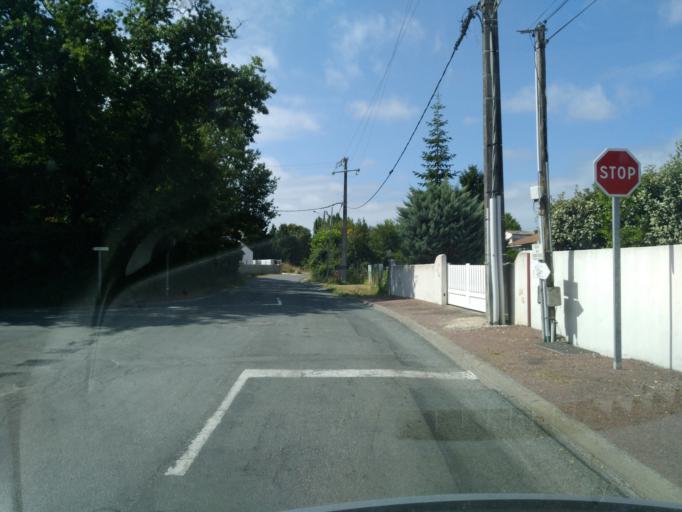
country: FR
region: Poitou-Charentes
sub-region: Departement de la Charente-Maritime
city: Breuillet
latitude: 45.6960
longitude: -1.0668
